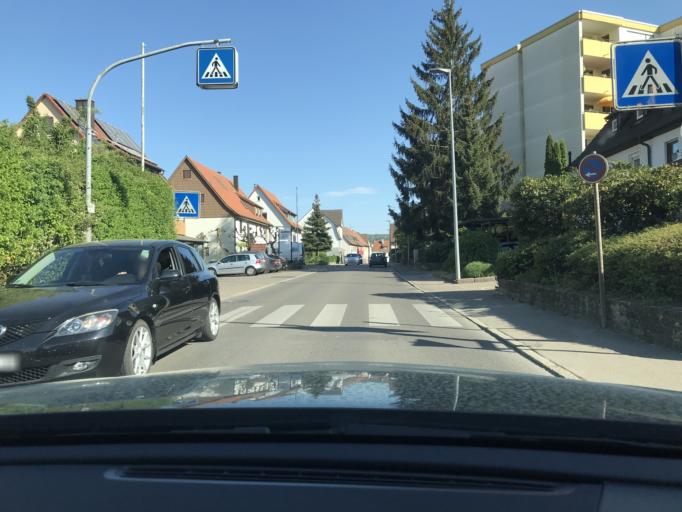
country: DE
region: Baden-Wuerttemberg
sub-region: Regierungsbezirk Stuttgart
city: Weinstadt-Endersbach
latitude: 48.8040
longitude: 9.3845
